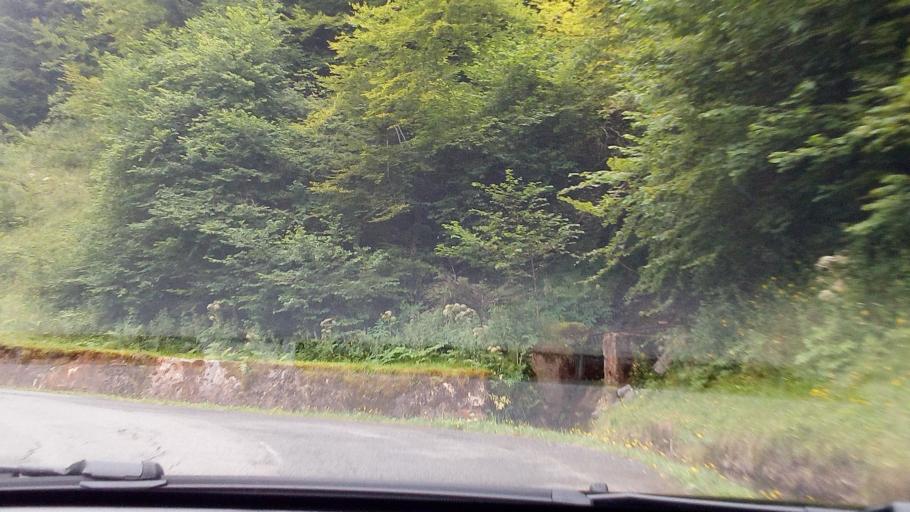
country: FR
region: Aquitaine
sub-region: Departement des Pyrenees-Atlantiques
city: Ogeu-les-Bains
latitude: 43.0703
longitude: -0.5123
